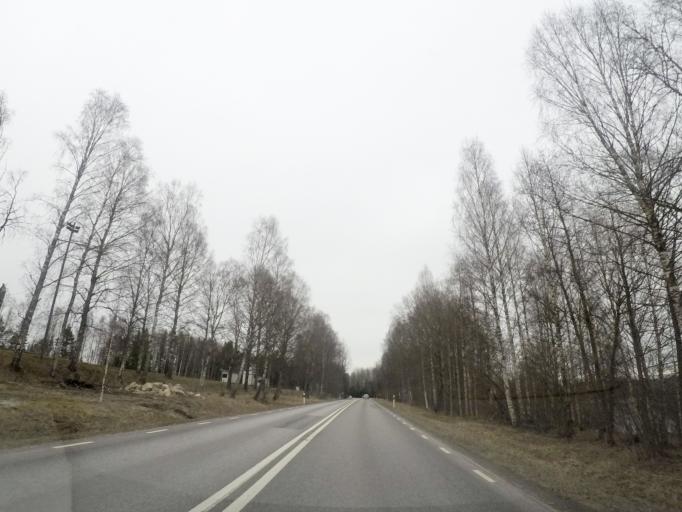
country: SE
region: Vaestmanland
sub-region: Skinnskattebergs Kommun
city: Skinnskatteberg
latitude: 59.8366
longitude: 15.6789
